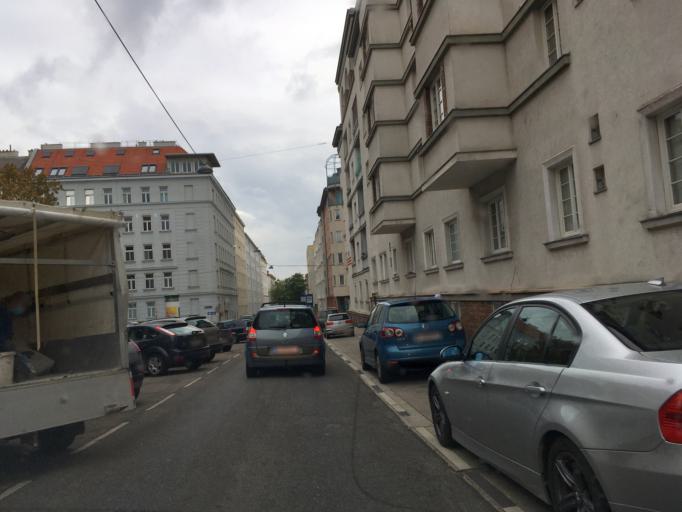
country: AT
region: Vienna
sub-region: Wien Stadt
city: Vienna
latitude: 48.1677
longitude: 16.3670
